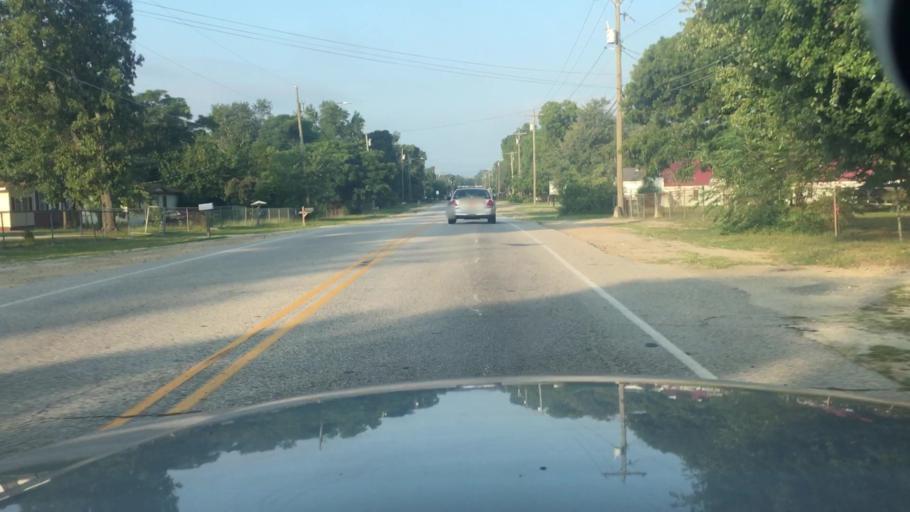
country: US
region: North Carolina
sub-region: Cumberland County
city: Spring Lake
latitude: 35.1128
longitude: -78.9324
